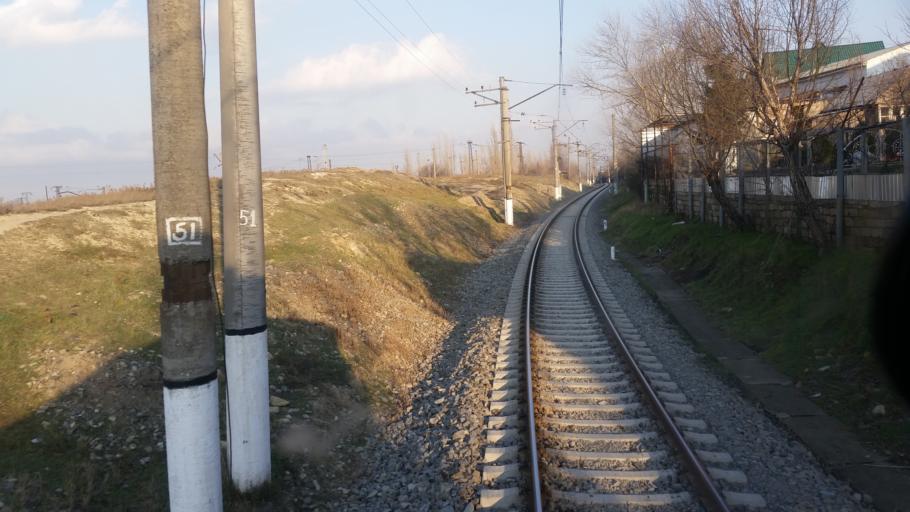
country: AZ
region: Baki
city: Bilajari
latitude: 40.4315
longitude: 49.7924
